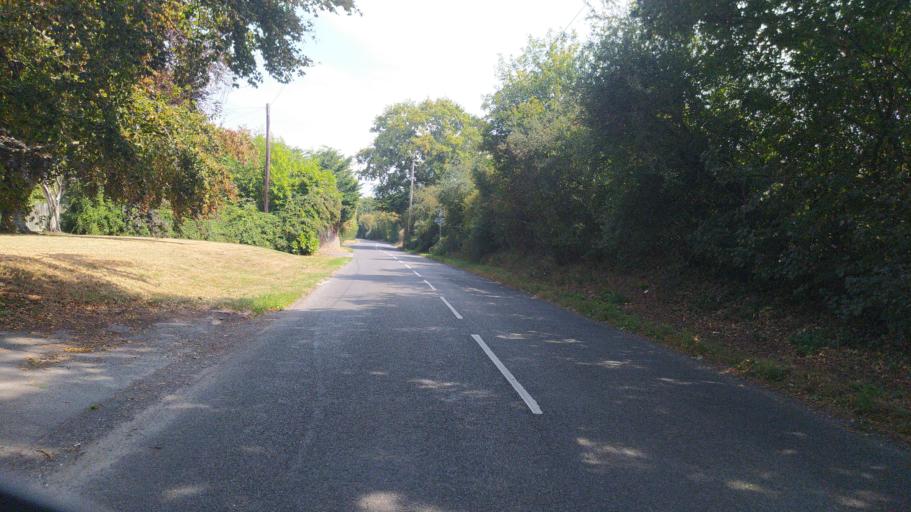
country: GB
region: England
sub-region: Hampshire
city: Emsworth
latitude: 50.8615
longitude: -0.9581
